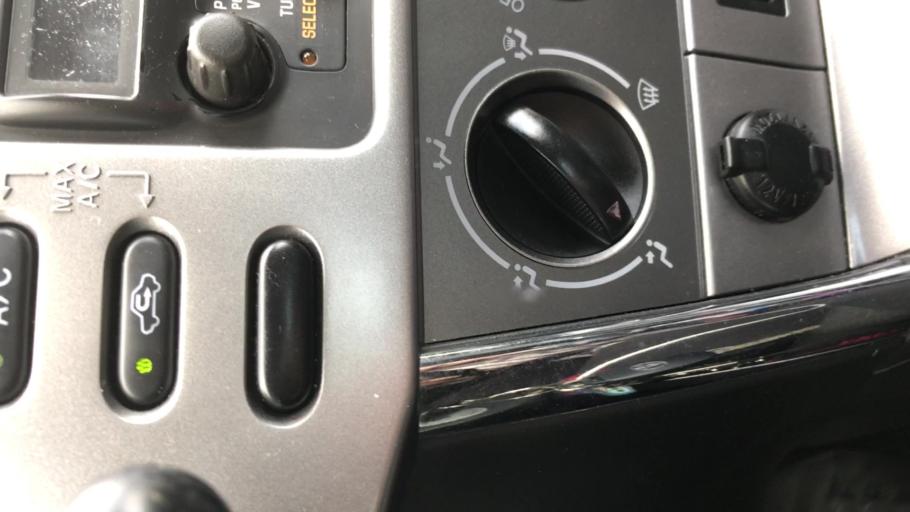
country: US
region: Virginia
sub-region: Prince William County
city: West Gate
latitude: 38.7763
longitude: -77.4992
